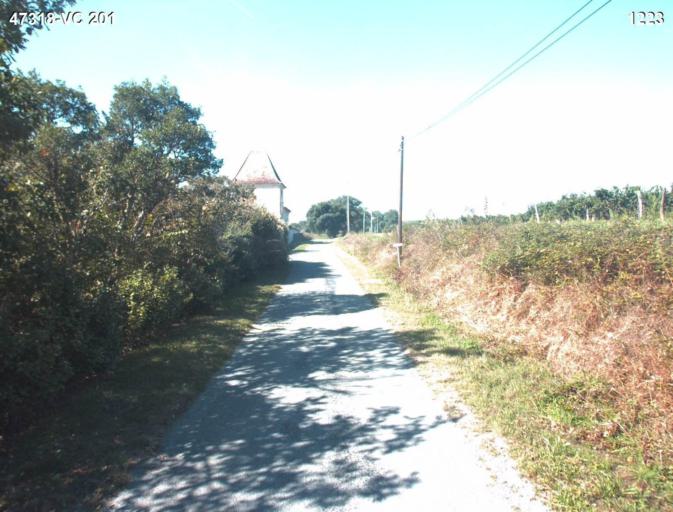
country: FR
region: Aquitaine
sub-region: Departement du Lot-et-Garonne
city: Vianne
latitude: 44.2076
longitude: 0.3147
